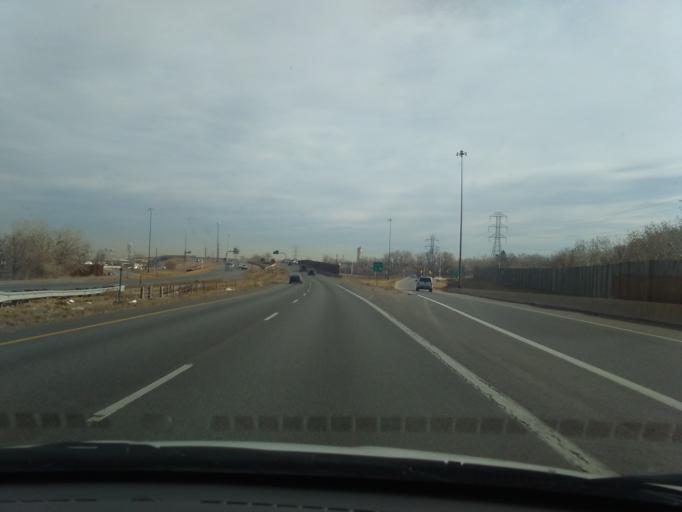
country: US
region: Colorado
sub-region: Adams County
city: Berkley
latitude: 39.7995
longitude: -105.0298
